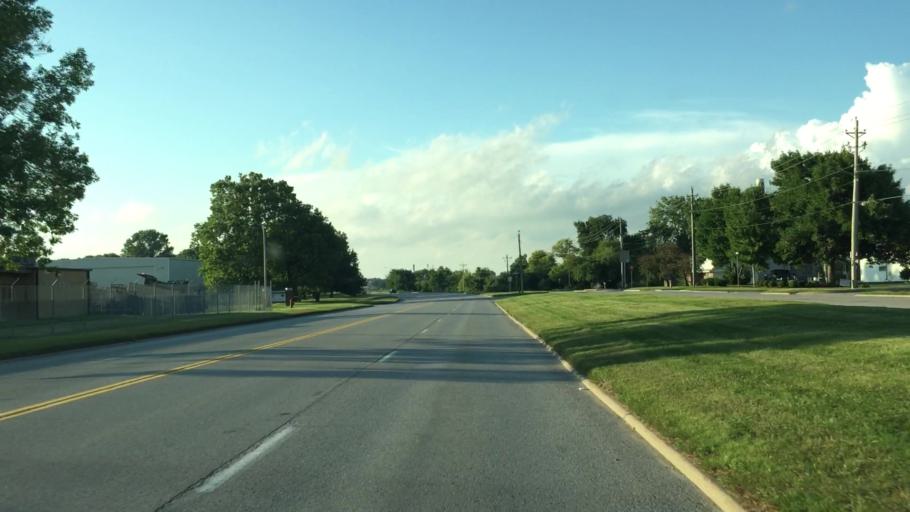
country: US
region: Iowa
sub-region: Johnson County
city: Iowa City
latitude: 41.6369
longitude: -91.5385
